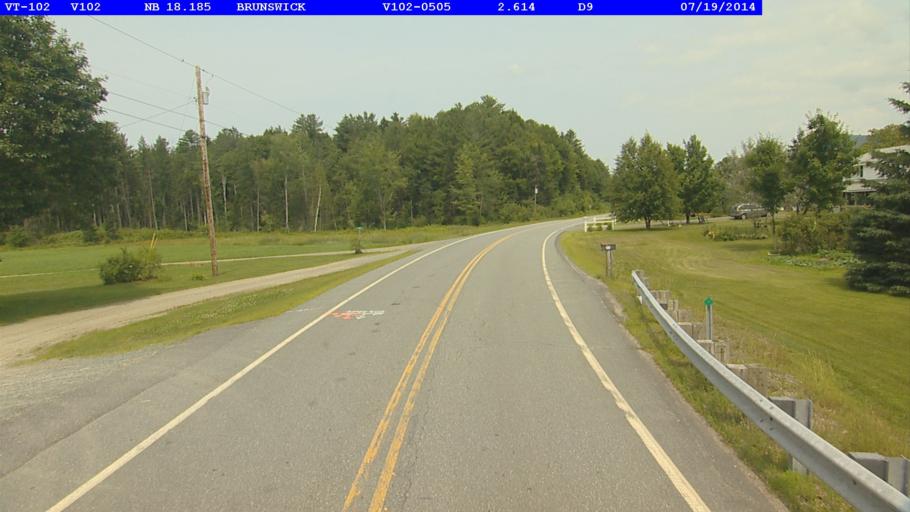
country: US
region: New Hampshire
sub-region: Coos County
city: Stratford
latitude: 44.6968
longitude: -71.6031
